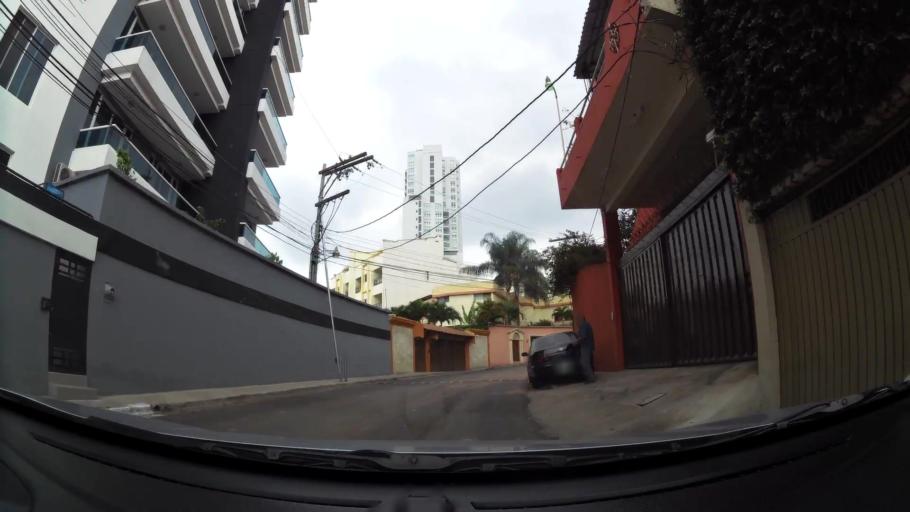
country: HN
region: Francisco Morazan
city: Tegucigalpa
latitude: 14.0922
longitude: -87.1860
